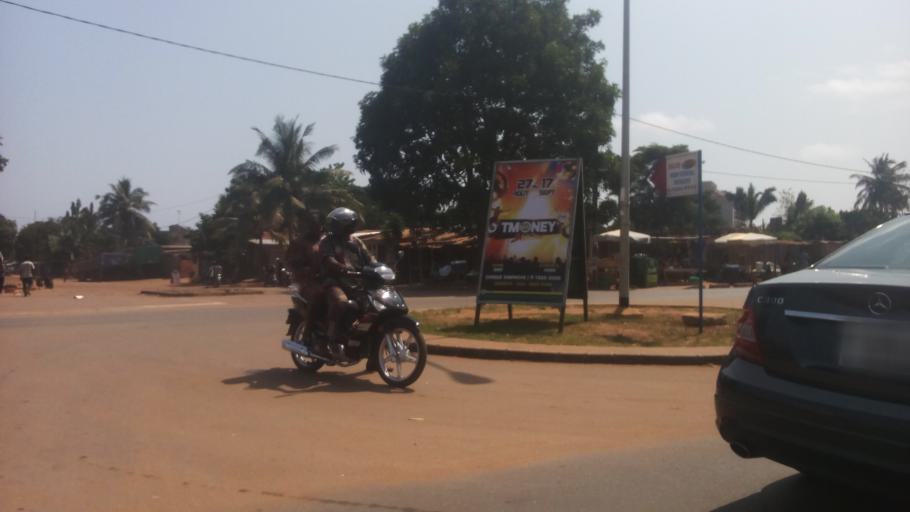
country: TG
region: Maritime
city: Lome
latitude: 6.1896
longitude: 1.2526
